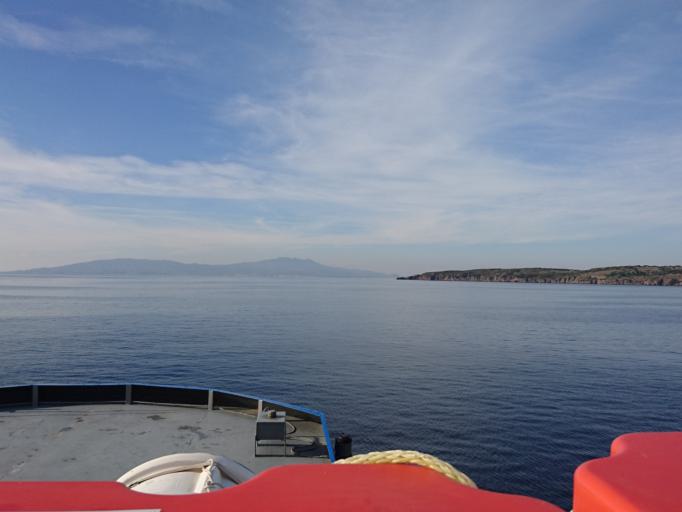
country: TR
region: Mugla
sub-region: Bodrum
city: Bodrum
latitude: 37.0020
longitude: 27.4040
